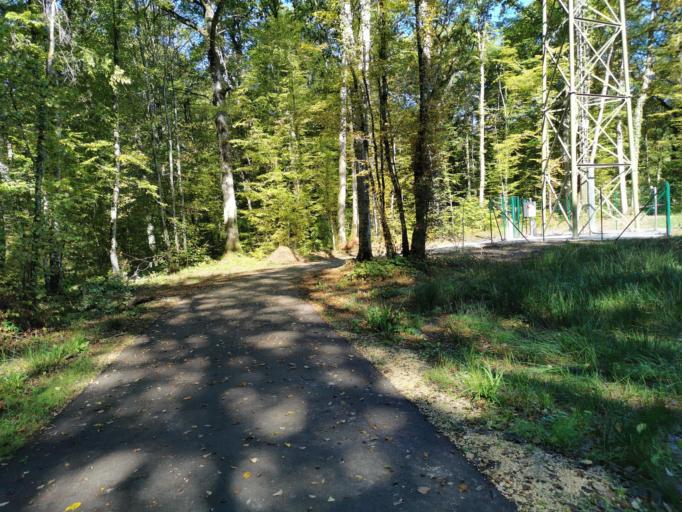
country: FR
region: Champagne-Ardenne
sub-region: Departement de l'Aube
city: Vendeuvre-sur-Barse
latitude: 48.2887
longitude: 4.3906
